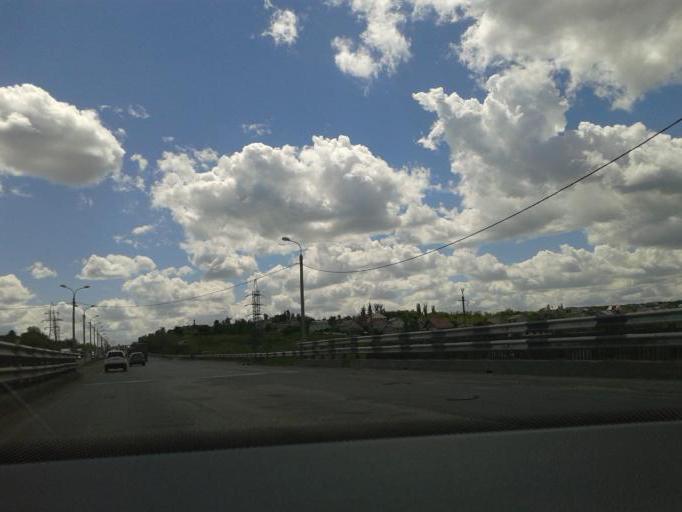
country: RU
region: Volgograd
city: Volgograd
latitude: 48.7147
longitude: 44.4436
